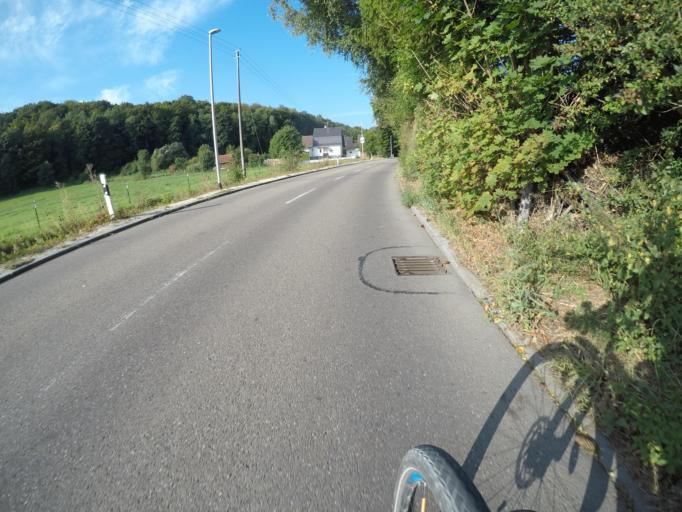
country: DE
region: Baden-Wuerttemberg
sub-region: Regierungsbezirk Stuttgart
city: Bolheim
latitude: 48.6174
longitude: 10.1511
